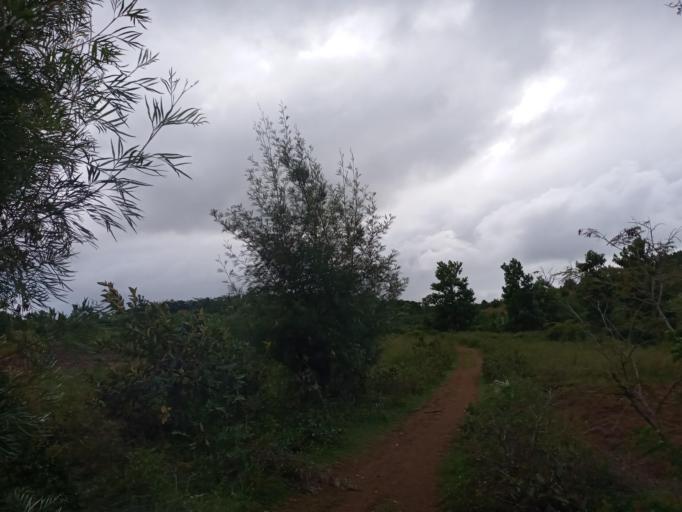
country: MG
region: Atsimo-Atsinanana
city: Vohipaho
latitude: -23.7745
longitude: 47.5357
